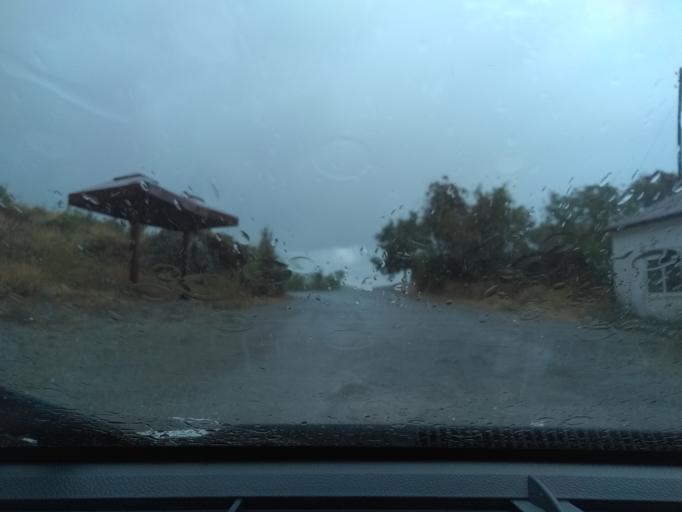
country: ME
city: Stari Bar
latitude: 42.1733
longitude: 19.1876
